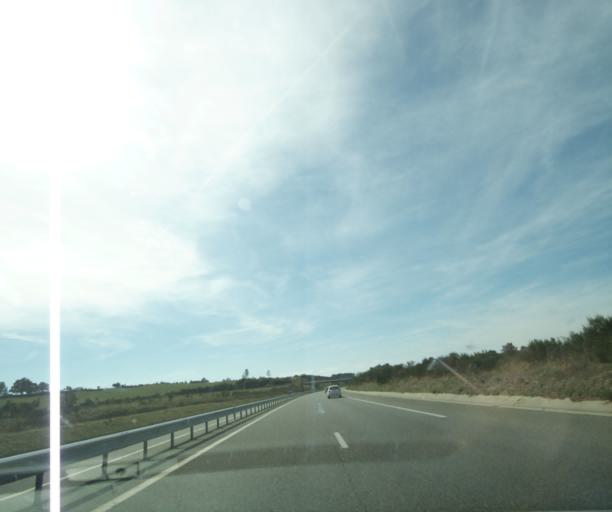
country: FR
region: Auvergne
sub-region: Departement du Puy-de-Dome
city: Saint-Ours
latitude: 45.8873
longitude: 2.9286
